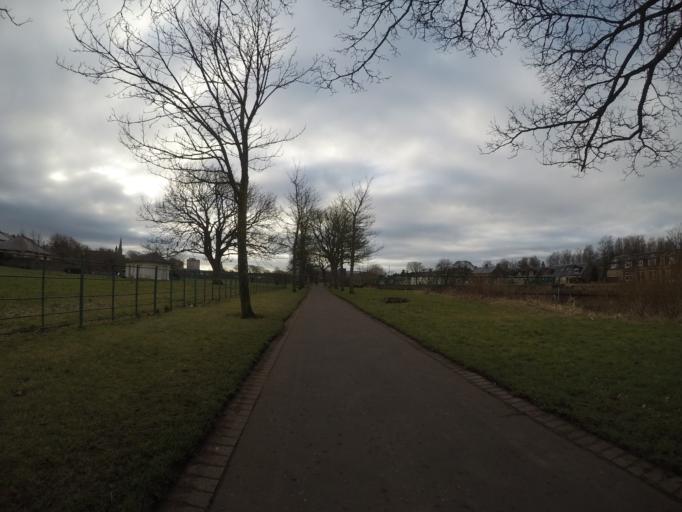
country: GB
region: Scotland
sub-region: North Ayrshire
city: Irvine
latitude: 55.6174
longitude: -4.6737
